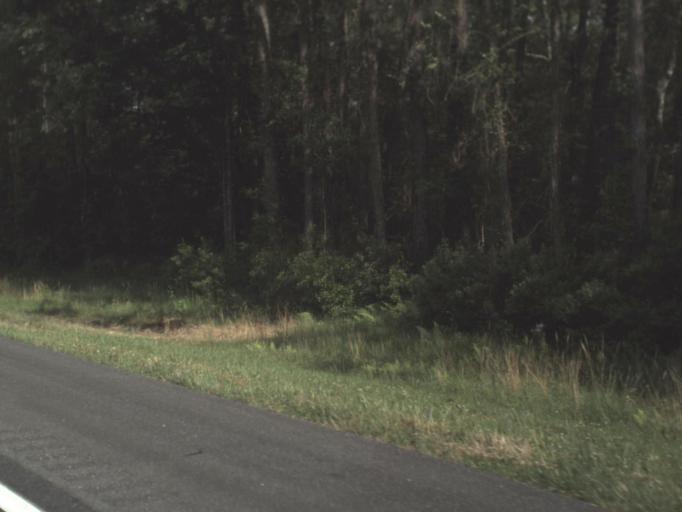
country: US
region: Florida
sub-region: Baker County
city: Macclenny
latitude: 30.2383
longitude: -82.2658
